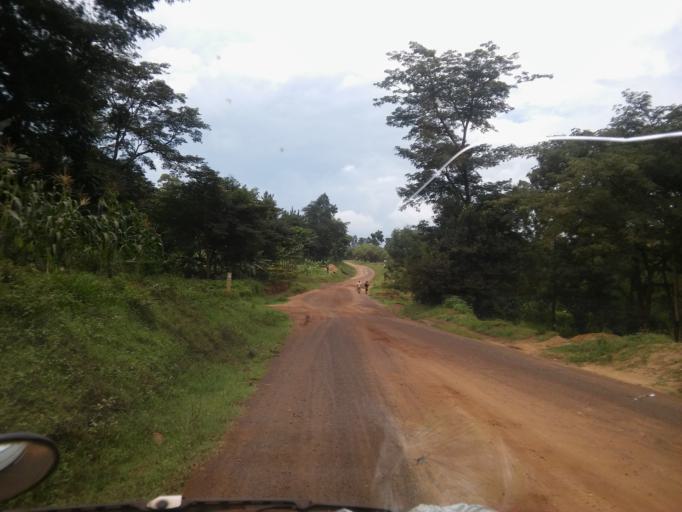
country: UG
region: Eastern Region
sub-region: Bududa District
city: Bududa
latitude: 0.9508
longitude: 34.2646
